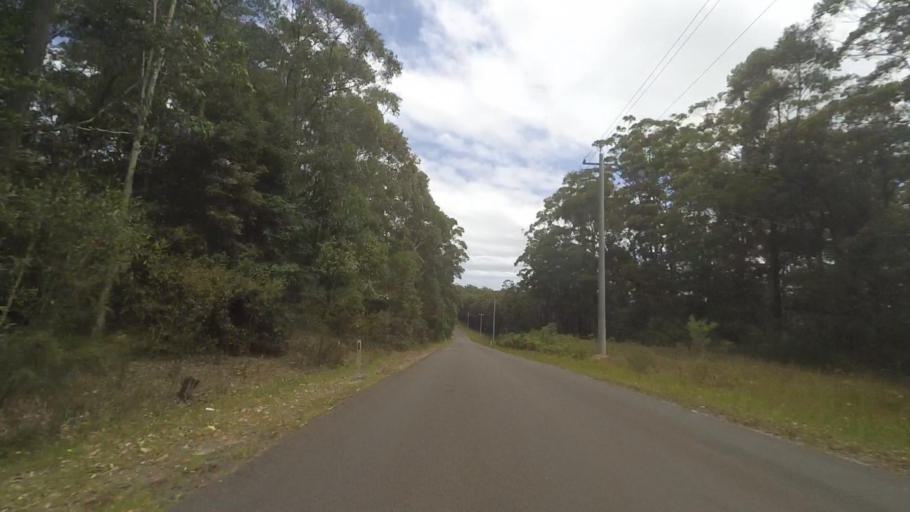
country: AU
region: New South Wales
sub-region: Shoalhaven Shire
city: Milton
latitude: -35.3779
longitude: 150.3748
